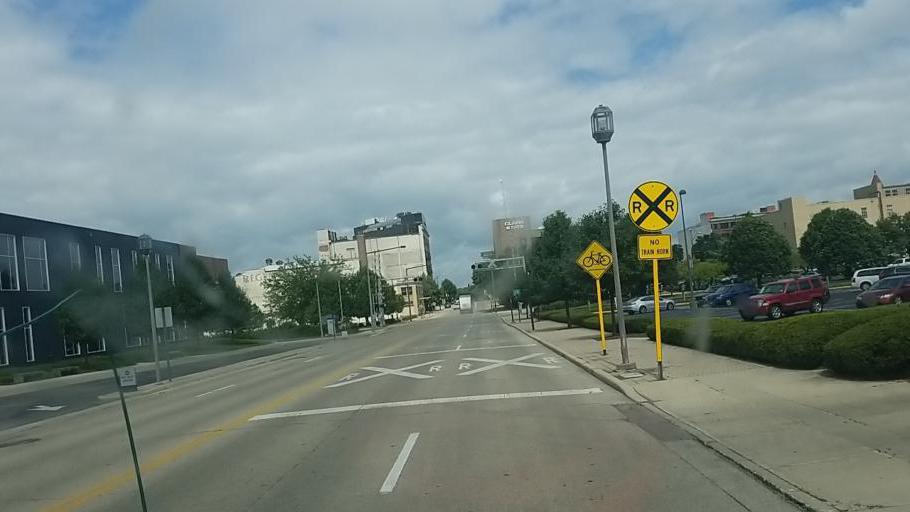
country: US
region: Ohio
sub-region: Clark County
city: Springfield
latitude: 39.9210
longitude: -83.8087
